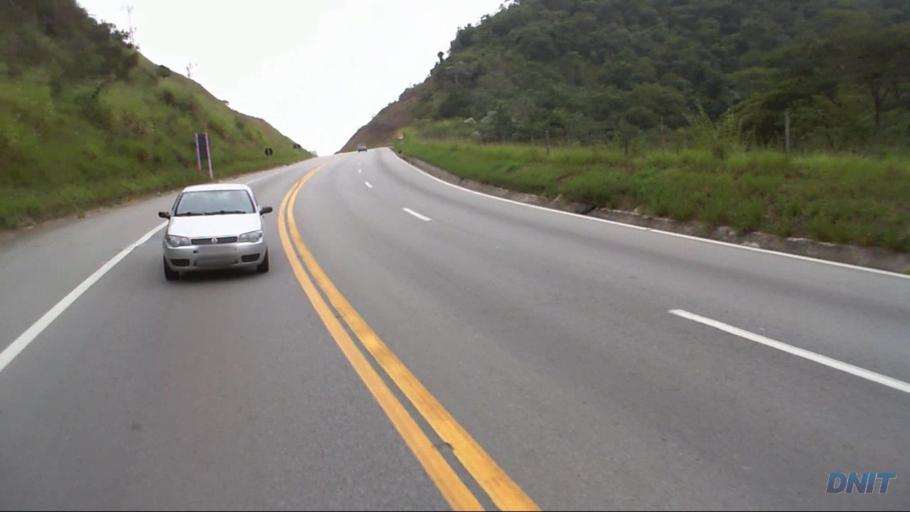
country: BR
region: Minas Gerais
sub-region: Nova Era
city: Nova Era
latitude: -19.6520
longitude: -42.9492
